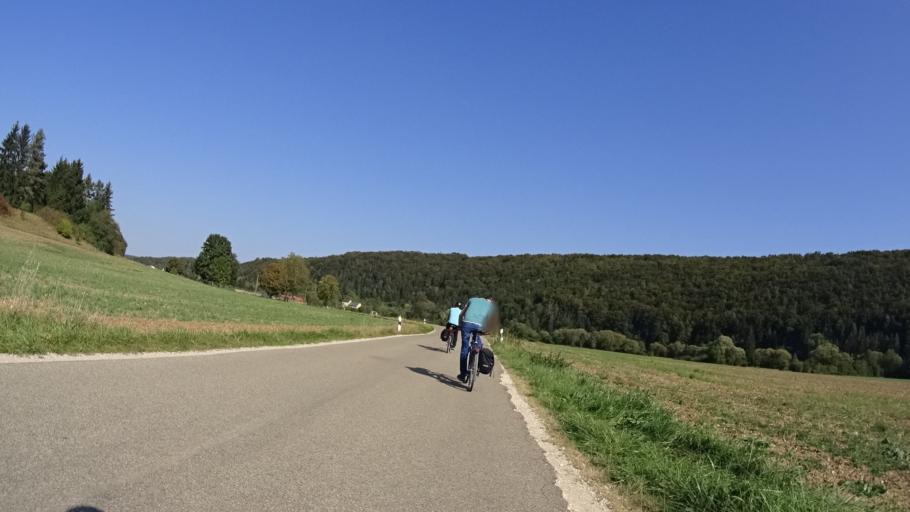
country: DE
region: Bavaria
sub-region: Upper Bavaria
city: Walting
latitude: 48.9077
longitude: 11.2953
